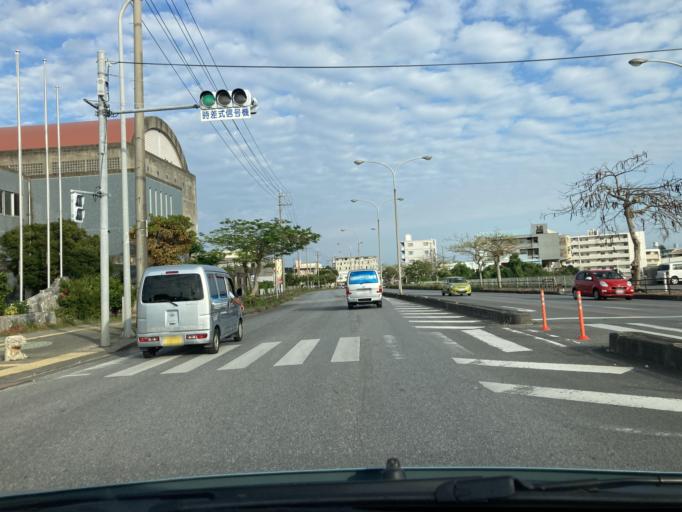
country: JP
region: Okinawa
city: Okinawa
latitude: 26.3534
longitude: 127.8092
